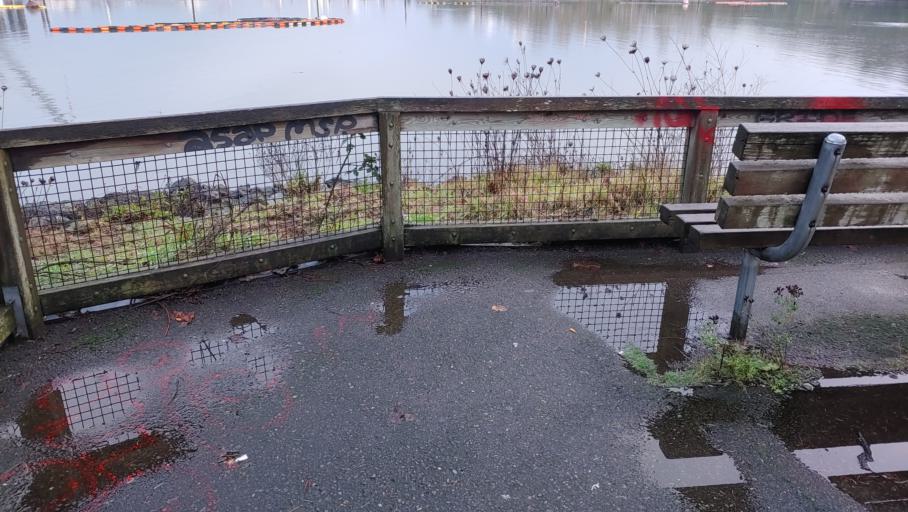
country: US
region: Washington
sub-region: King County
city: White Center
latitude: 47.5612
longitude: -122.3502
